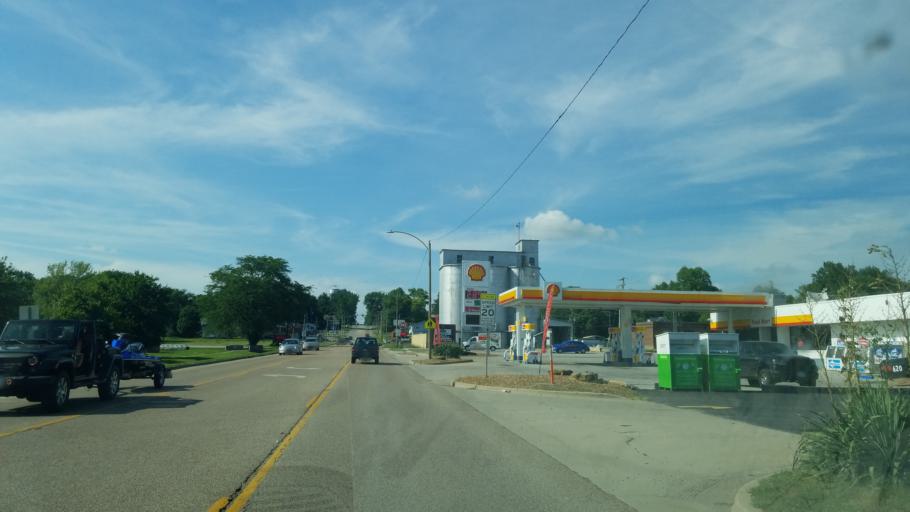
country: US
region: Illinois
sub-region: Saint Clair County
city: Lebanon
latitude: 38.5988
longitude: -89.8076
